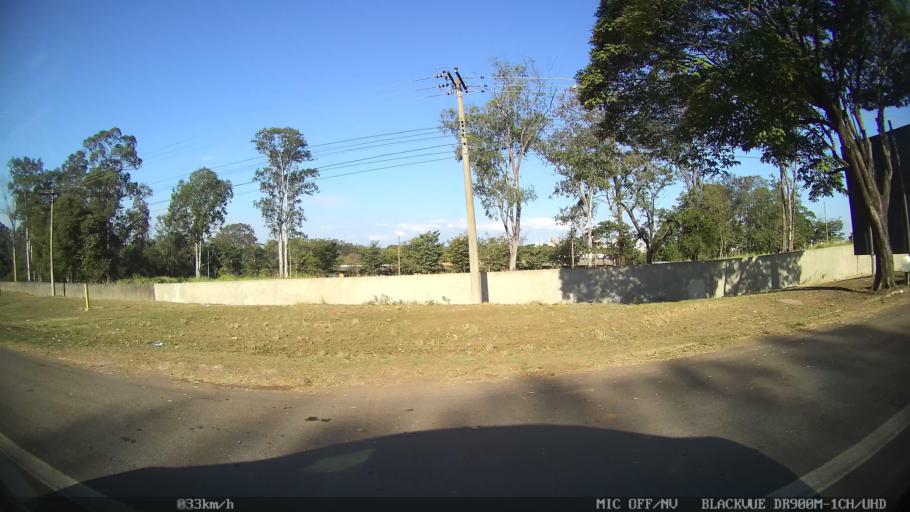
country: BR
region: Sao Paulo
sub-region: Piracicaba
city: Piracicaba
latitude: -22.6981
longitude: -47.6531
